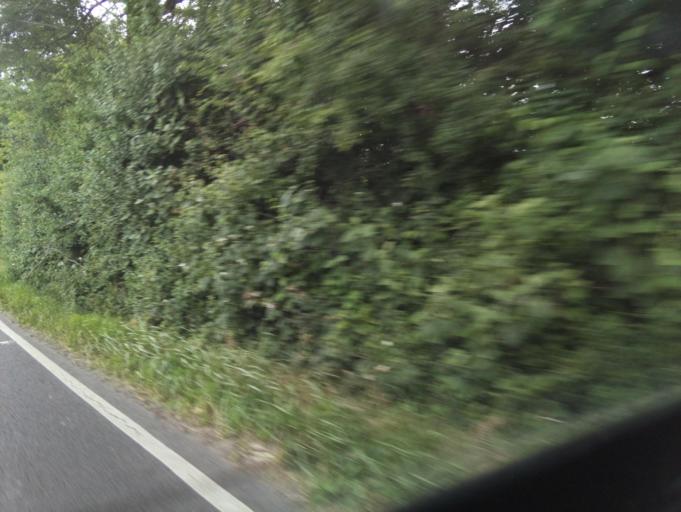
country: GB
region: England
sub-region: Somerset
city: Merriott
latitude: 50.9056
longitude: -2.7479
